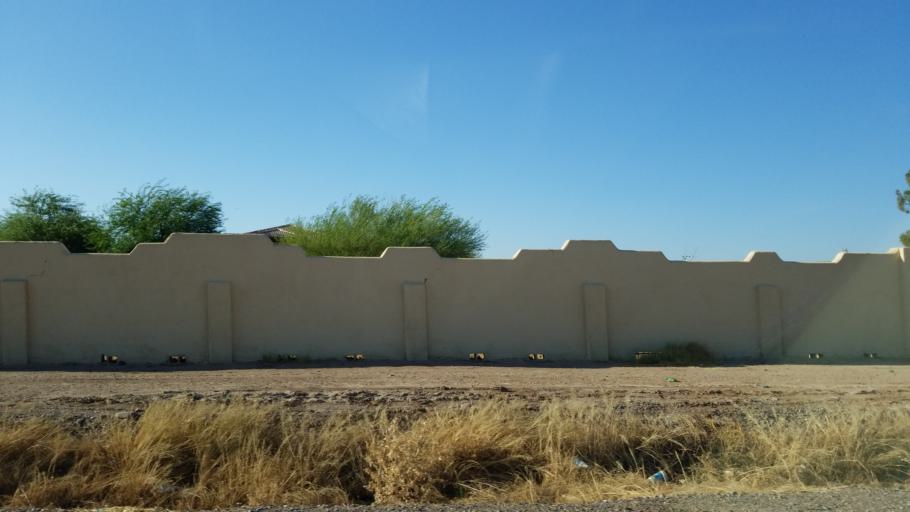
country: US
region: Arizona
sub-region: Maricopa County
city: Laveen
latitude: 33.3774
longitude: -112.2077
